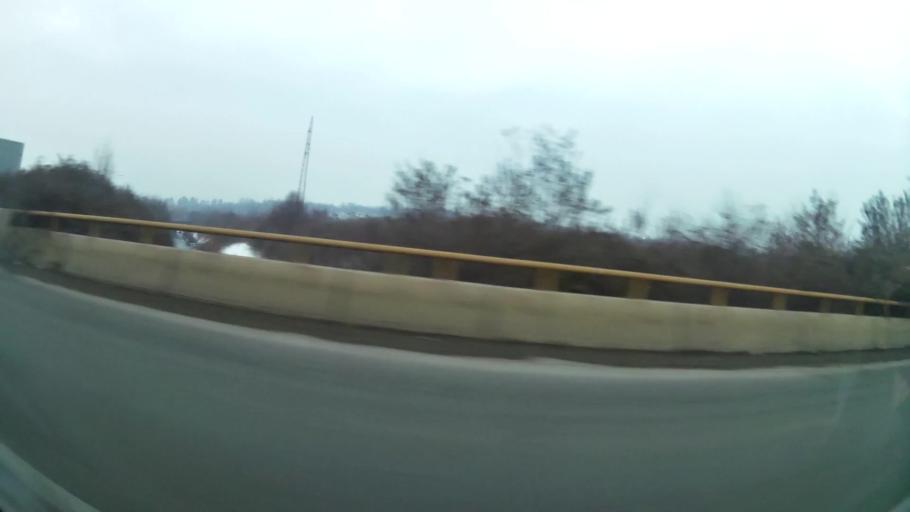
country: MK
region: Suto Orizari
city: Suto Orizare
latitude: 42.0195
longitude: 21.4102
